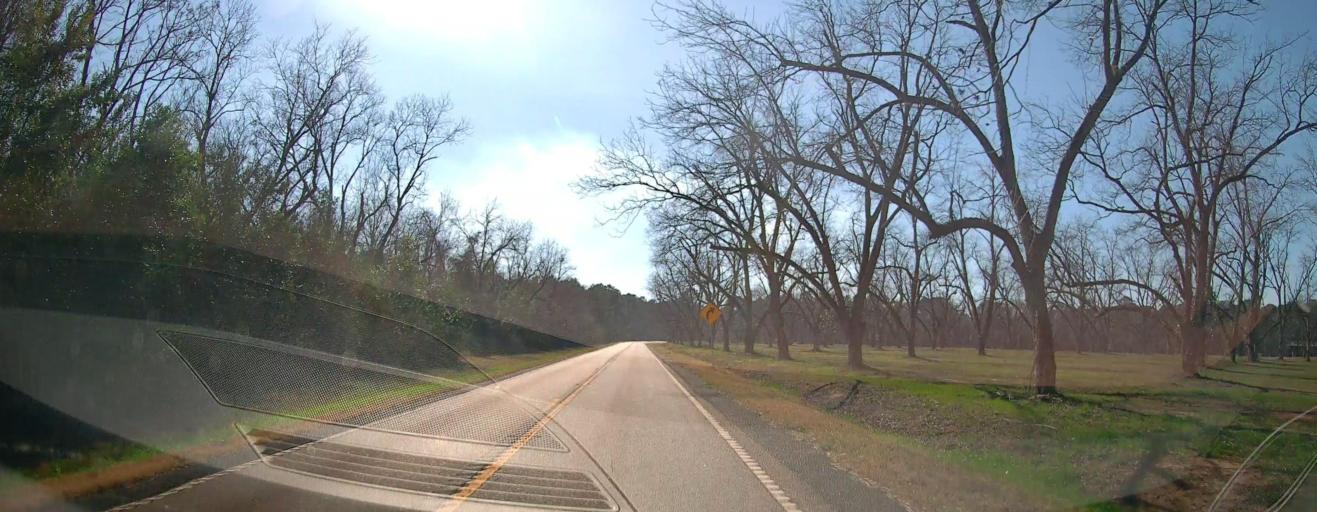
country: US
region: Georgia
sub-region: Sumter County
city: Americus
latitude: 32.1895
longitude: -84.1627
